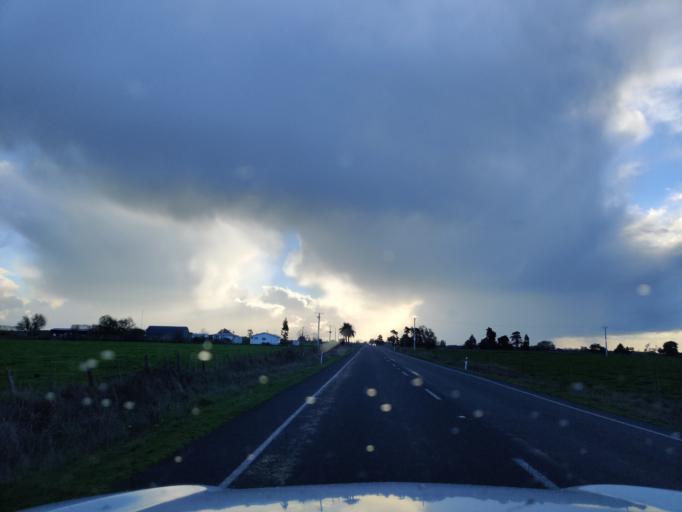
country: NZ
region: Waikato
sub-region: Hamilton City
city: Hamilton
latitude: -37.6925
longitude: 175.4299
